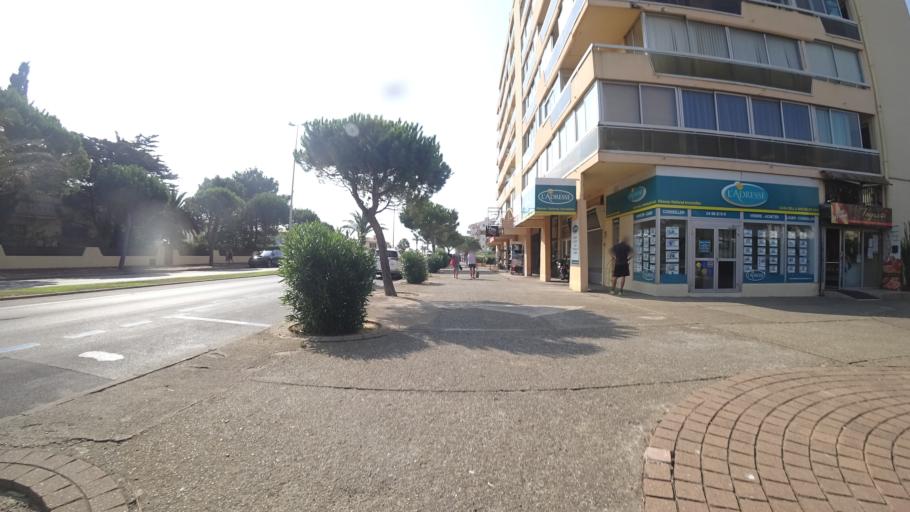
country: FR
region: Languedoc-Roussillon
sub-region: Departement des Pyrenees-Orientales
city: Saint-Cyprien-Plage
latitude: 42.6247
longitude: 3.0350
